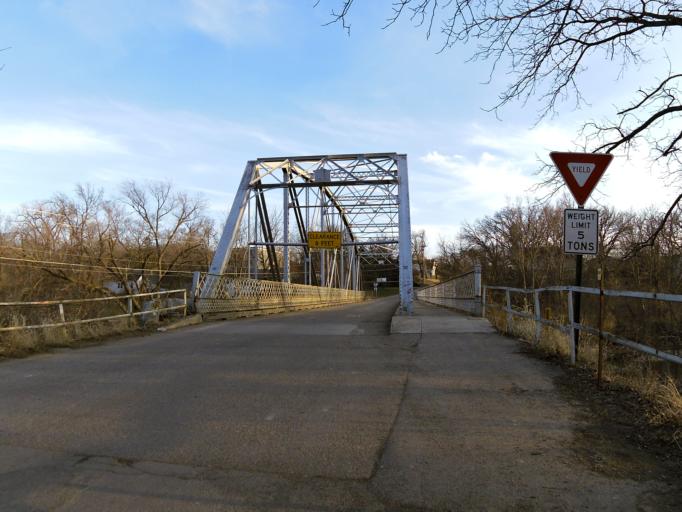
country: US
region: Minnesota
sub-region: Goodhue County
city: Cannon Falls
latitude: 44.5138
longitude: -92.9044
